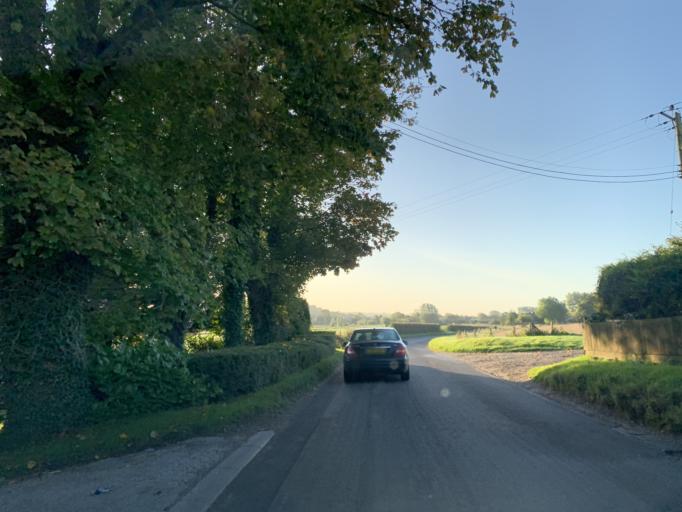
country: GB
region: England
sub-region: Wiltshire
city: Woodford
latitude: 51.1007
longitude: -1.8242
